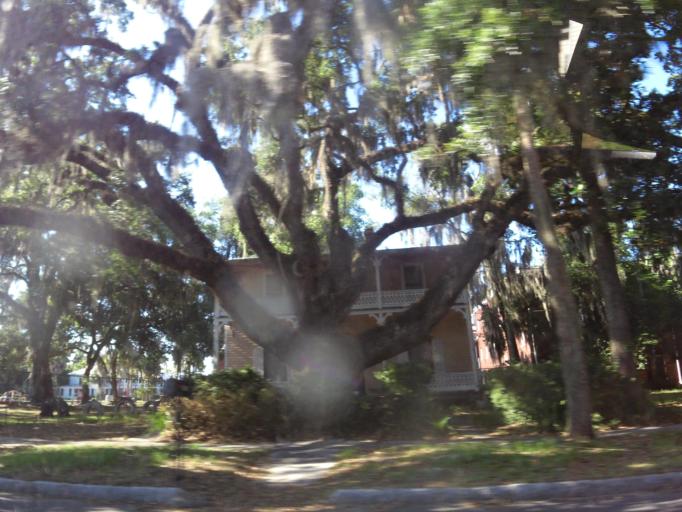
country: US
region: Florida
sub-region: Putnam County
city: Palatka
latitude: 29.6452
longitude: -81.6343
